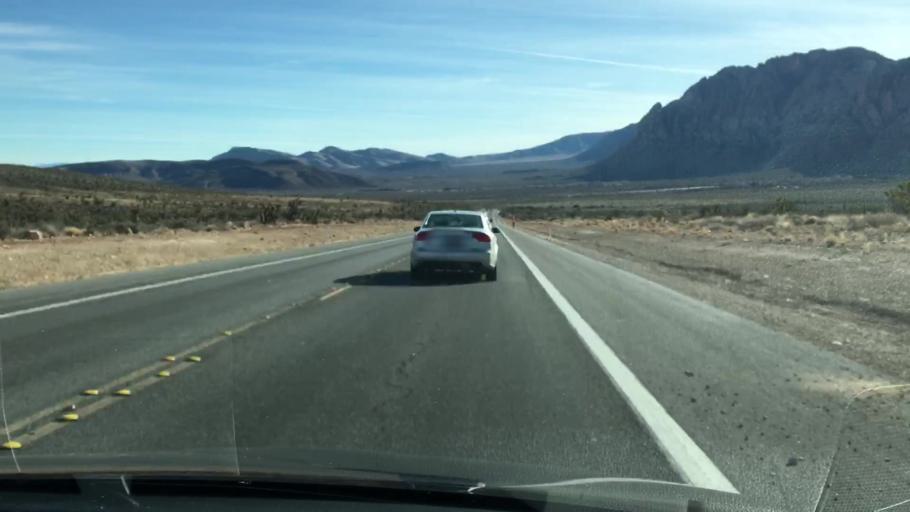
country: US
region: Nevada
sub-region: Clark County
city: Summerlin South
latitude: 36.0954
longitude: -115.4490
